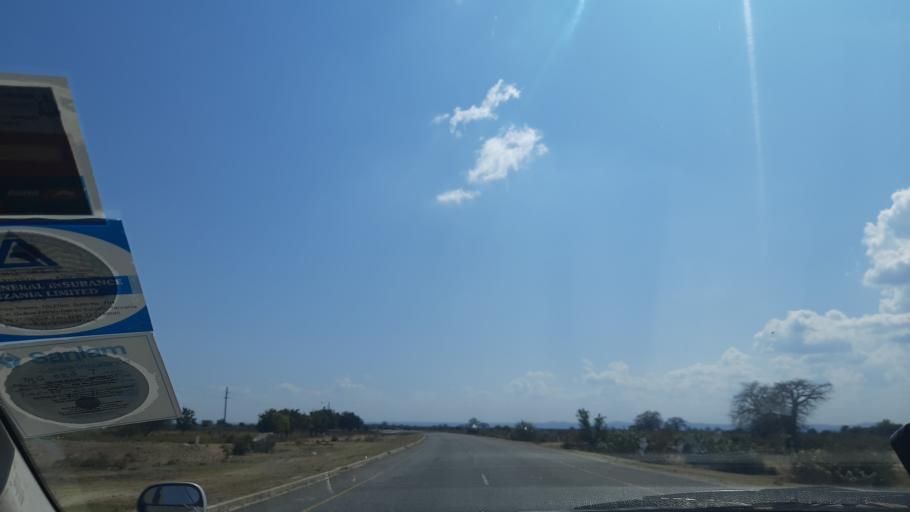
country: TZ
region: Singida
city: Kintinku
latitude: -5.8809
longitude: 35.1380
